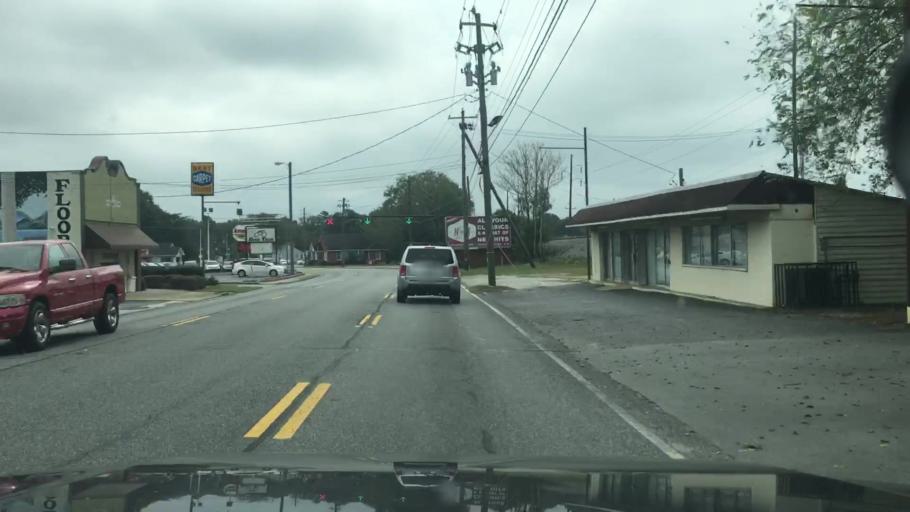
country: US
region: Georgia
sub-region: Bibb County
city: Macon
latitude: 32.8491
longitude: -83.6730
